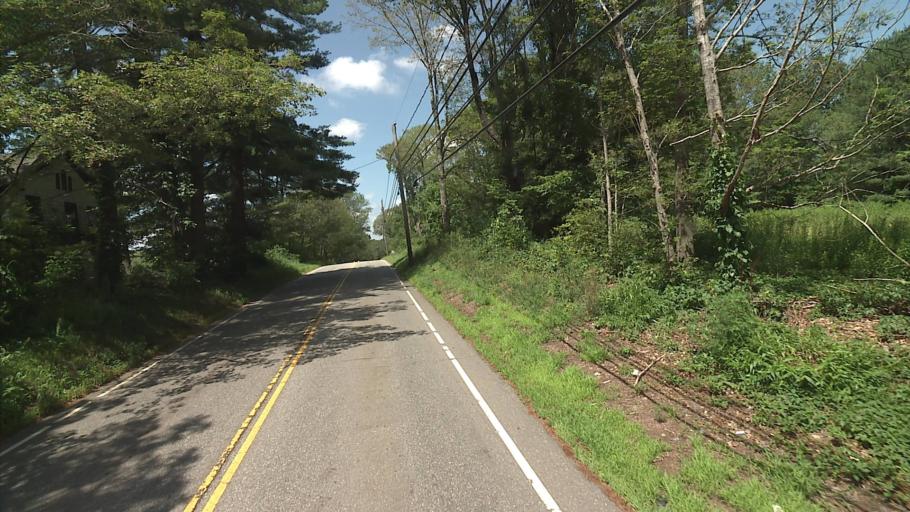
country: US
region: Connecticut
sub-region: Windham County
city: Windham
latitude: 41.6996
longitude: -72.1381
